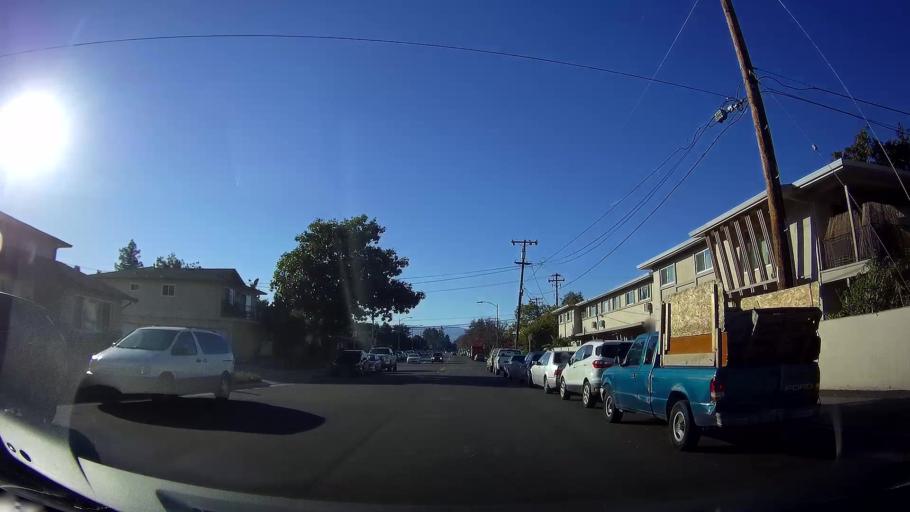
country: US
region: California
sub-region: Santa Clara County
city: Santa Clara
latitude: 37.3202
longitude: -121.9679
